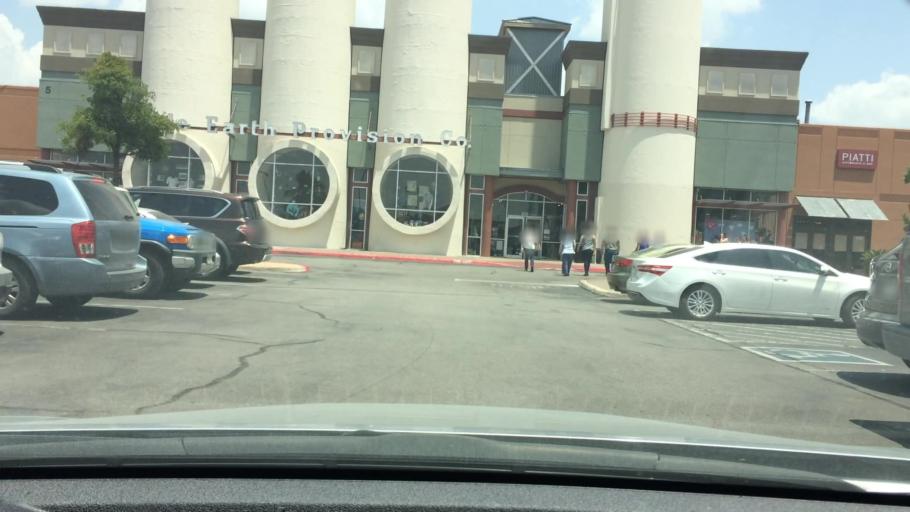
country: US
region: Texas
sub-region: Bexar County
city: Alamo Heights
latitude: 29.4962
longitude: -98.4803
